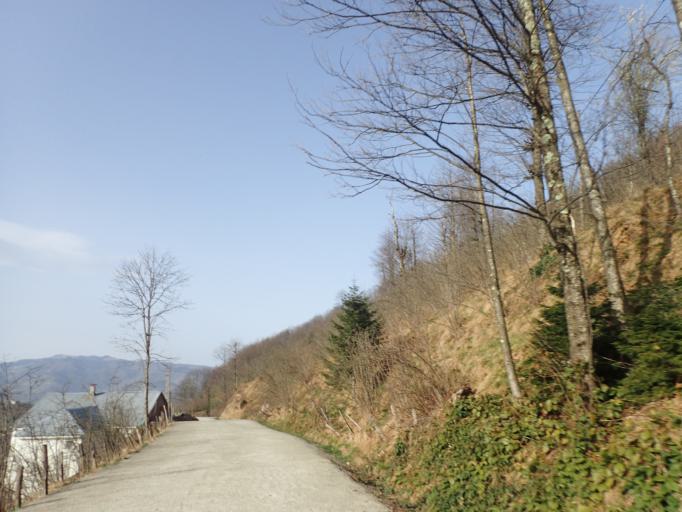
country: TR
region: Ordu
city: Kabaduz
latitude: 40.8209
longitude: 37.9031
